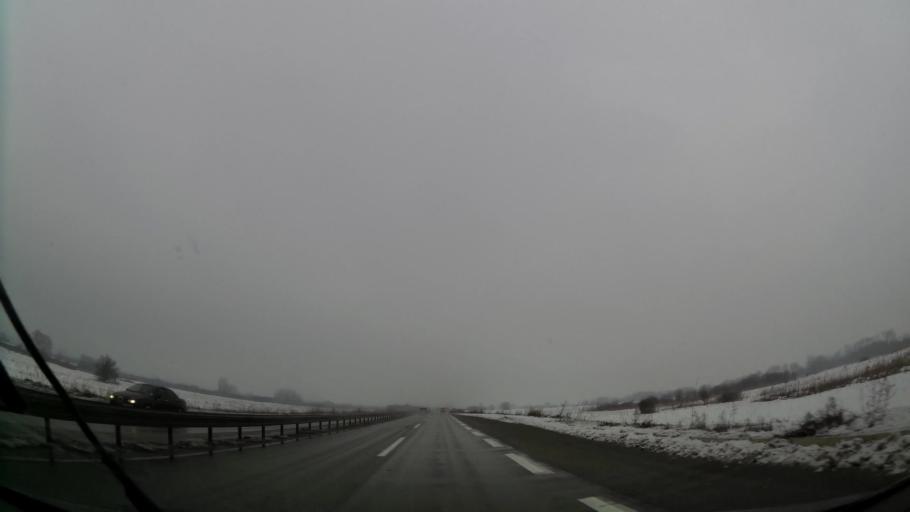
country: RS
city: Ostruznica
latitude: 44.7479
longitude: 20.3718
